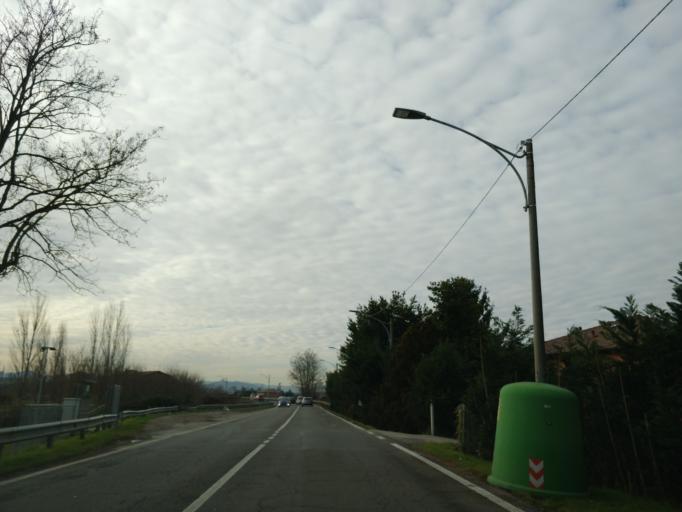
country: IT
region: Emilia-Romagna
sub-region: Provincia di Bologna
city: Progresso
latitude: 44.5441
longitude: 11.3743
